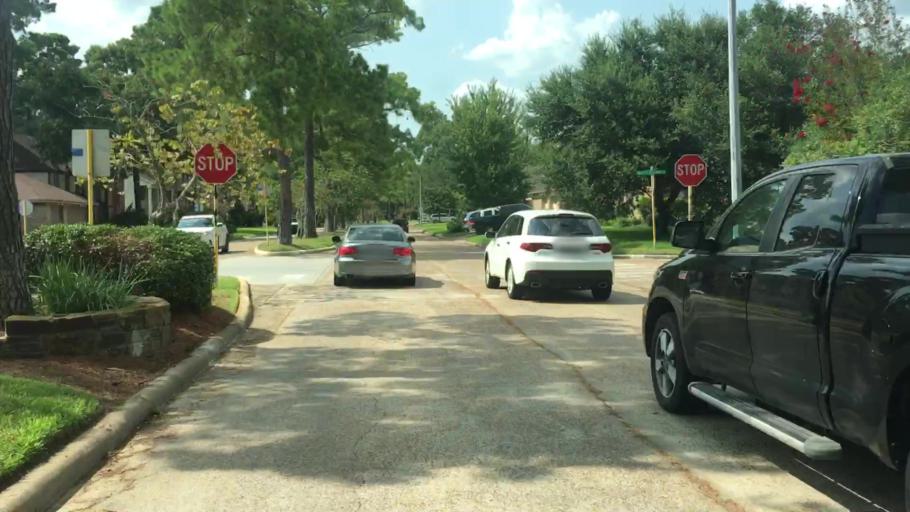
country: US
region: Texas
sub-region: Harris County
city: Atascocita
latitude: 30.0045
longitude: -95.1553
